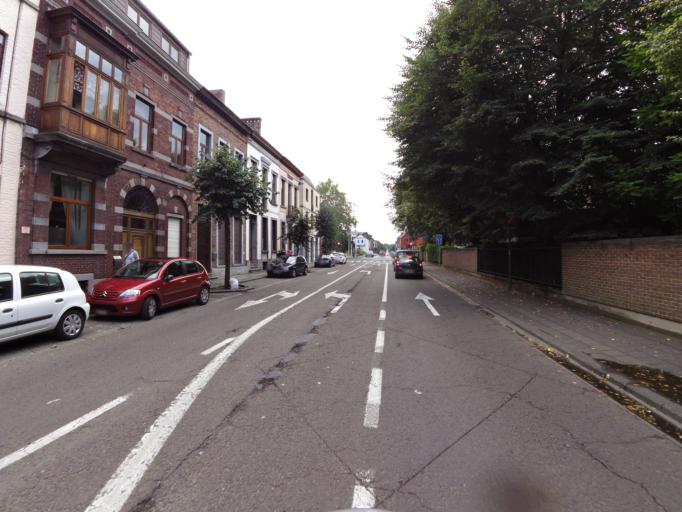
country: BE
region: Wallonia
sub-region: Province du Hainaut
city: Mons
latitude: 50.4493
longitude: 3.9543
